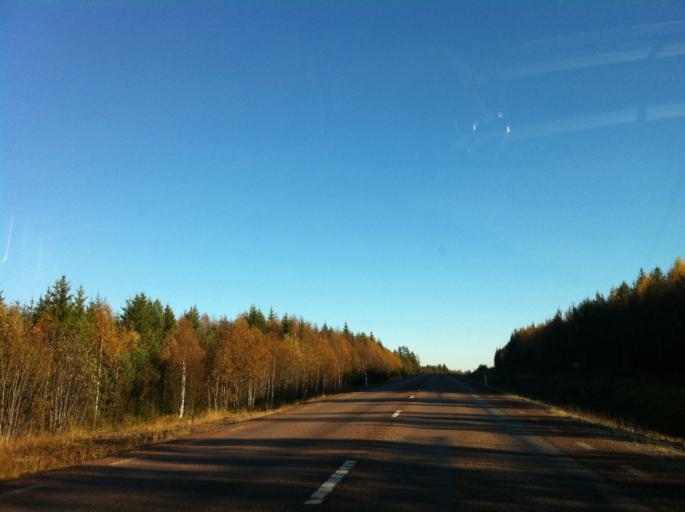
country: SE
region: Dalarna
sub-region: Rattviks Kommun
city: Raettvik
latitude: 60.8403
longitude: 15.2075
